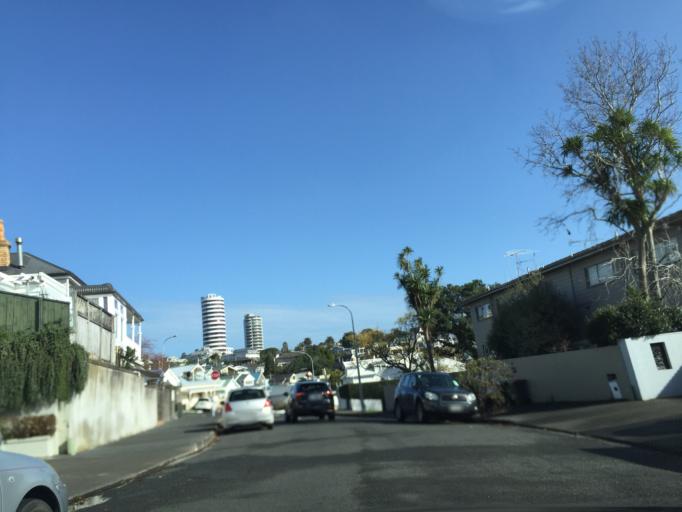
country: NZ
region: Auckland
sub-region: Auckland
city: Auckland
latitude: -36.8436
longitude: 174.7466
